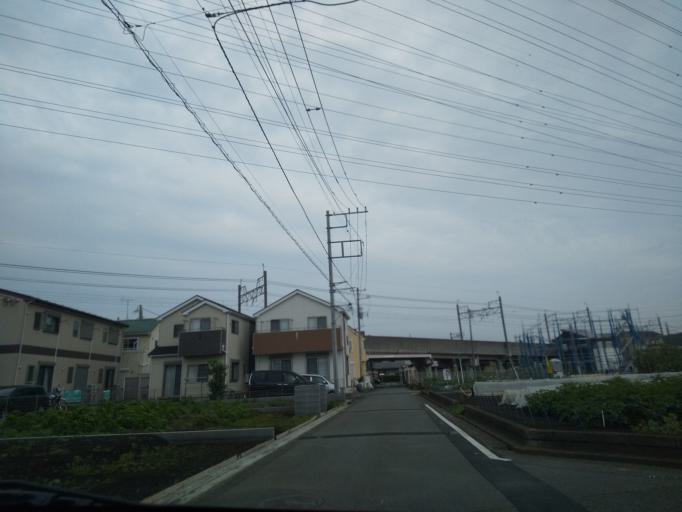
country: JP
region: Tokyo
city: Hachioji
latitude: 35.5960
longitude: 139.3607
